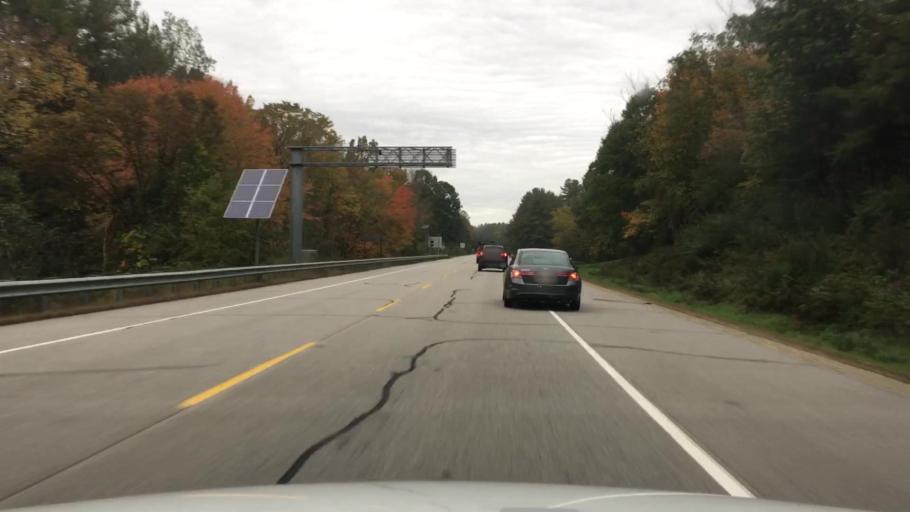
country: US
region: New Hampshire
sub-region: Strafford County
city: Durham
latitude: 43.1442
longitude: -70.9181
